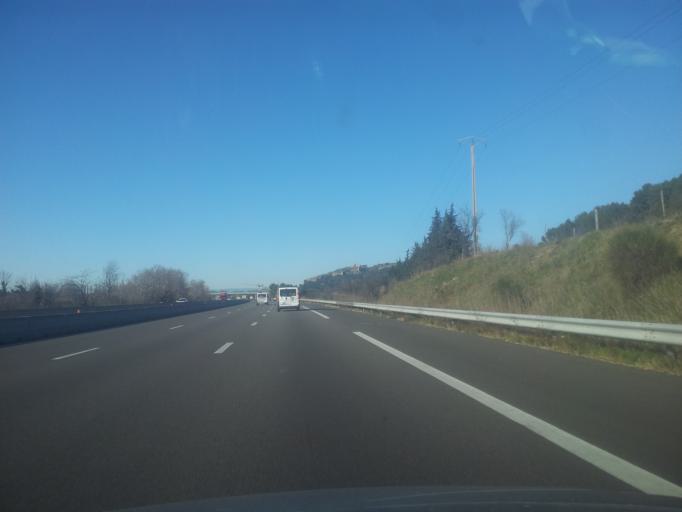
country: FR
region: Provence-Alpes-Cote d'Azur
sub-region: Departement du Vaucluse
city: Mornas
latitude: 44.1890
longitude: 4.7458
